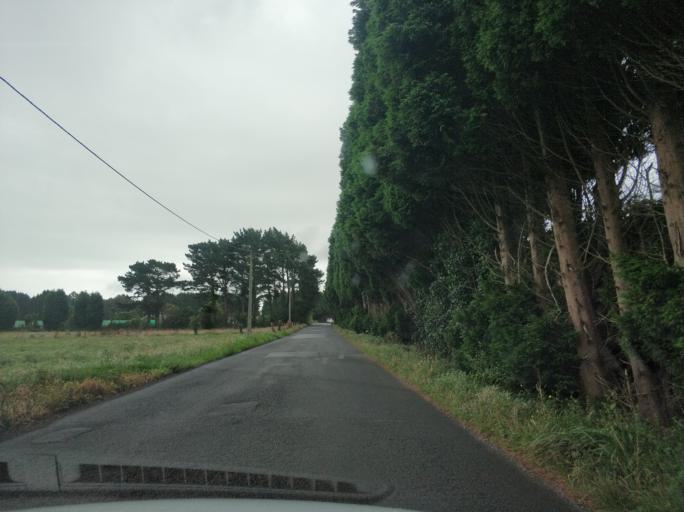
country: ES
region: Asturias
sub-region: Province of Asturias
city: Tineo
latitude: 43.5525
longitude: -6.4563
